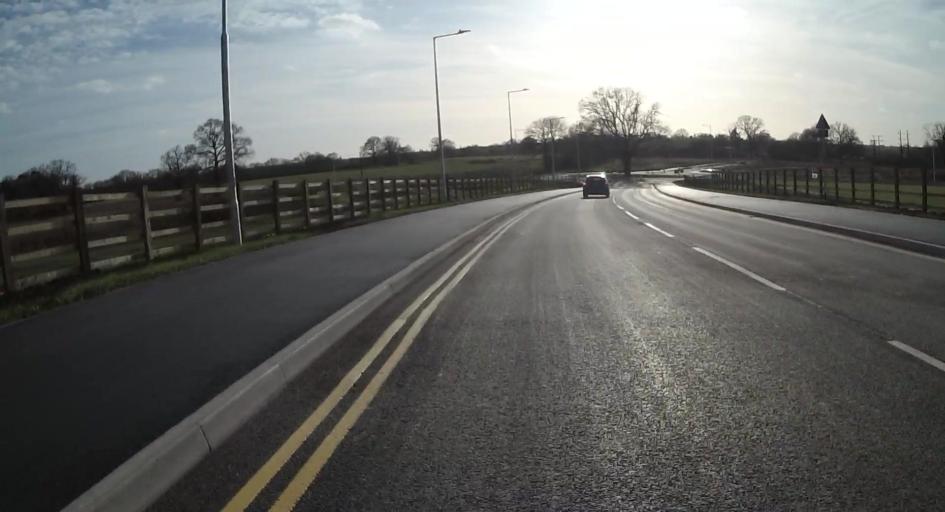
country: GB
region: England
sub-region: Wokingham
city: Wokingham
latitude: 51.4054
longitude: -0.8067
